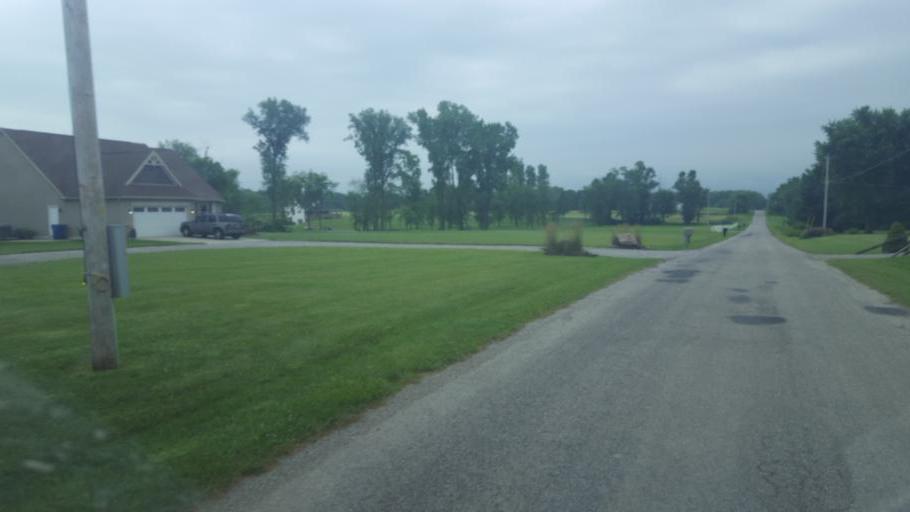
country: US
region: Ohio
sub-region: Knox County
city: Centerburg
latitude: 40.3709
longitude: -82.7824
